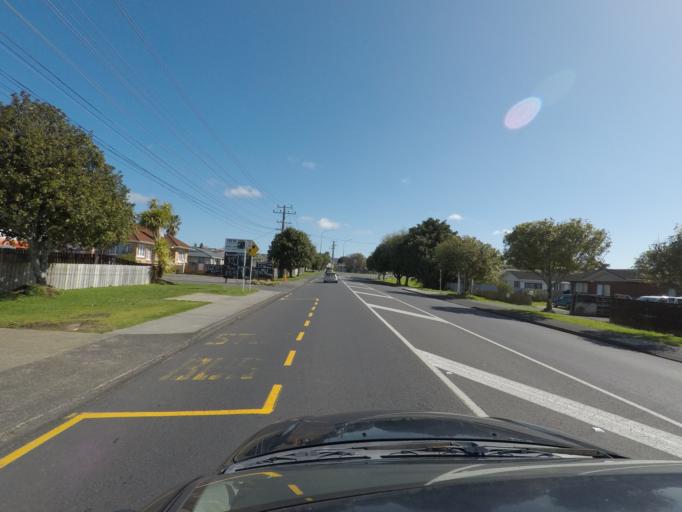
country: NZ
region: Auckland
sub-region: Auckland
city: Rosebank
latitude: -36.8629
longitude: 174.6066
